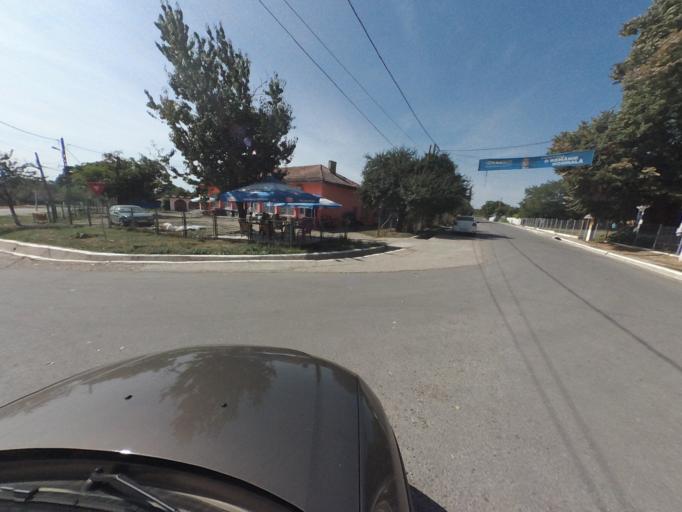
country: RO
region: Vaslui
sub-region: Comuna Deleni
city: Deleni
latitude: 46.5432
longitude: 27.7470
